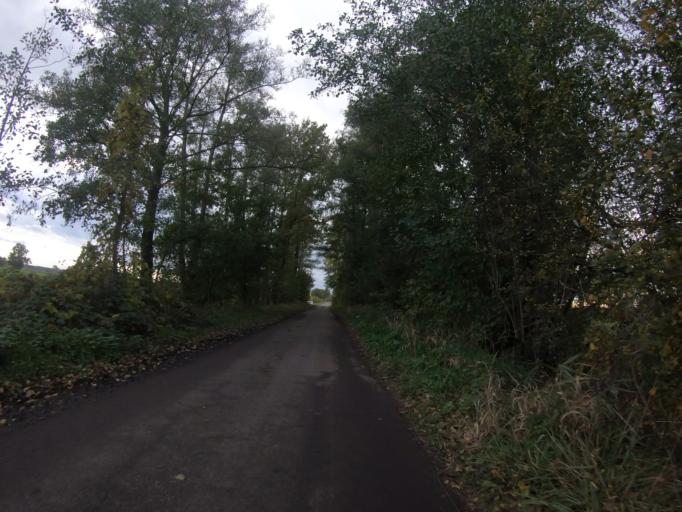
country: DE
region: Lower Saxony
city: Wagenhoff
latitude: 52.5404
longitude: 10.5471
